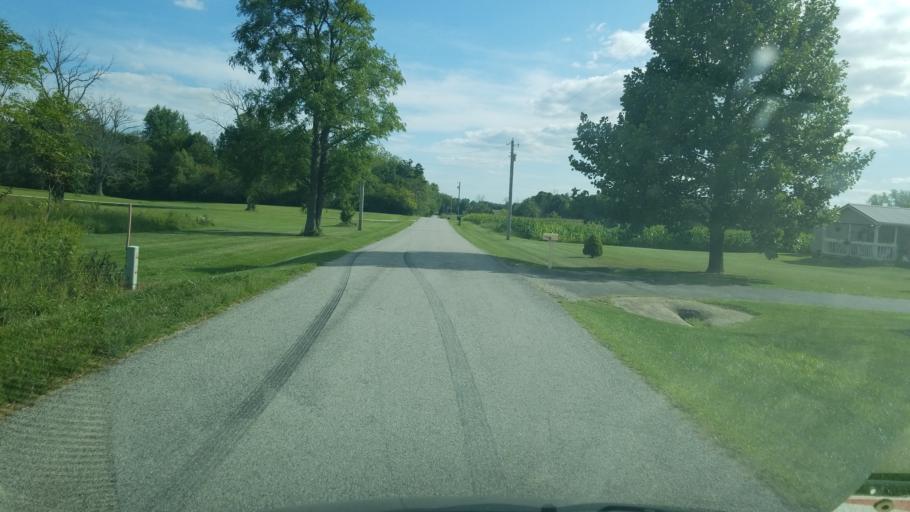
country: US
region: Ohio
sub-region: Champaign County
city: Saint Paris
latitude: 40.1400
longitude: -83.8729
